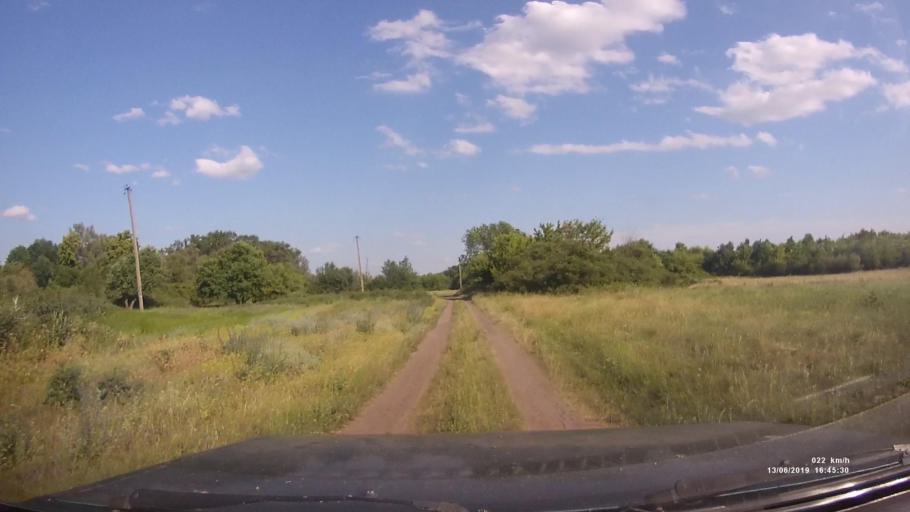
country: RU
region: Rostov
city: Kazanskaya
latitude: 49.9477
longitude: 41.4231
